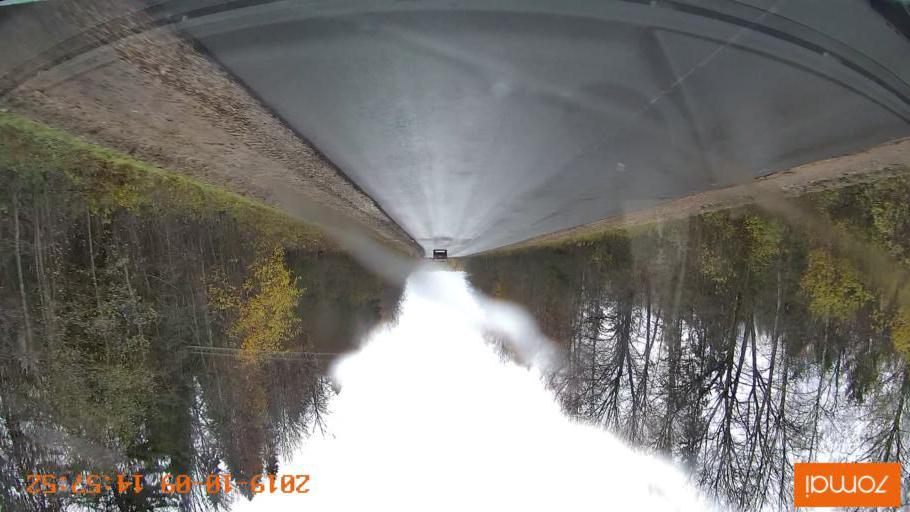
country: RU
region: Kostroma
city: Chistyye Bory
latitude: 58.3331
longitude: 41.6529
